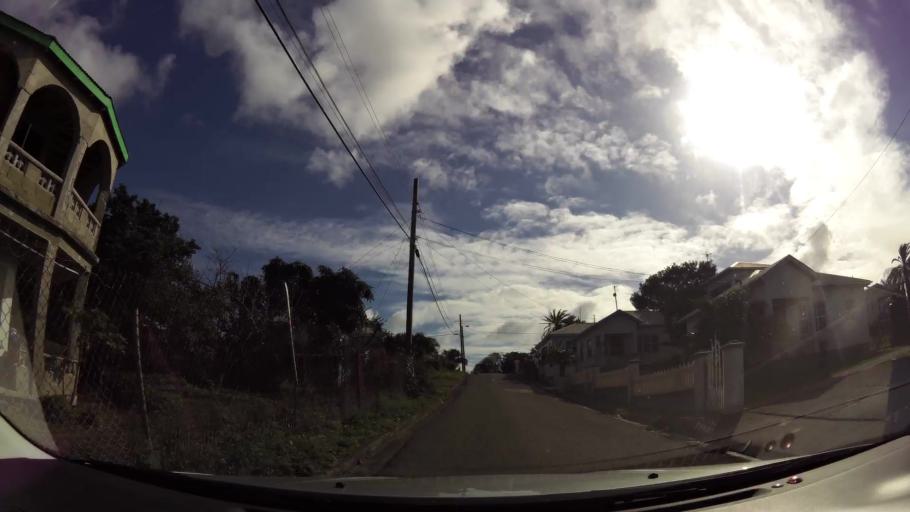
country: AG
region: Saint Peter
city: All Saints
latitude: 17.0681
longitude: -61.7909
